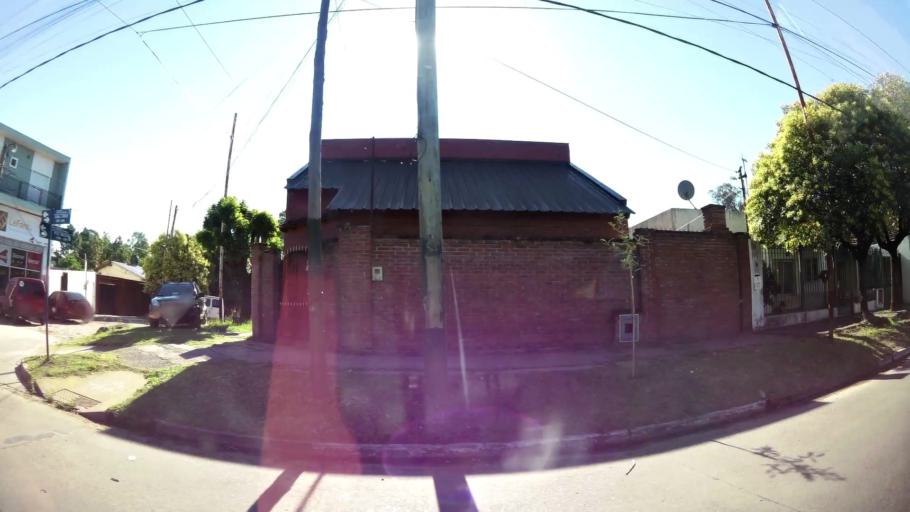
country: AR
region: Buenos Aires
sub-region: Partido de Lomas de Zamora
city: Lomas de Zamora
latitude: -34.7735
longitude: -58.4239
